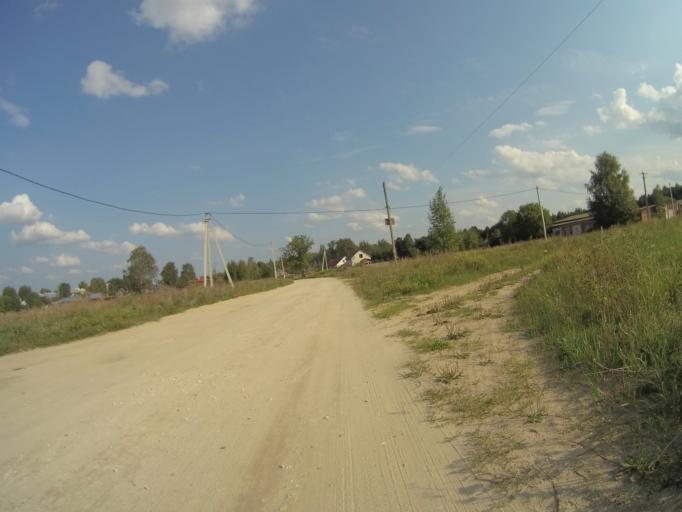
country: RU
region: Vladimir
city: Raduzhnyy
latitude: 56.0262
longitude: 40.3093
